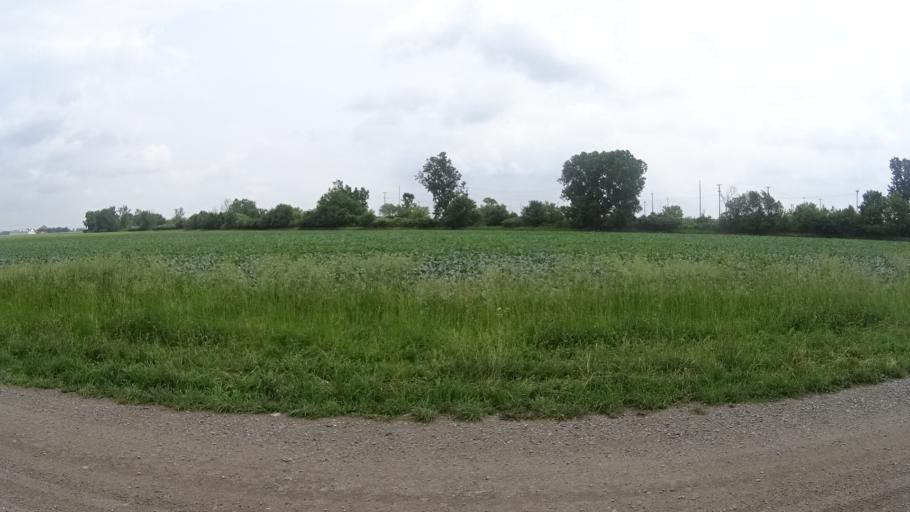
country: US
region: Ohio
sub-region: Huron County
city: Bellevue
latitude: 41.2918
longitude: -82.8042
